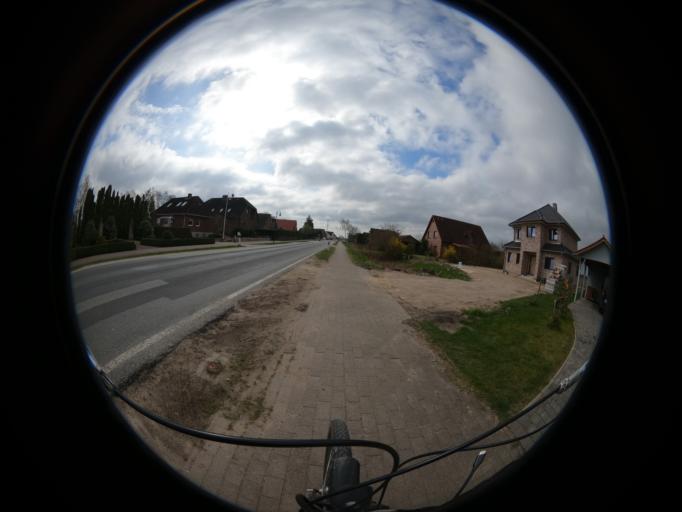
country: DE
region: Lower Saxony
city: Neu Wulmstorf
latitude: 53.4943
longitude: 9.7797
